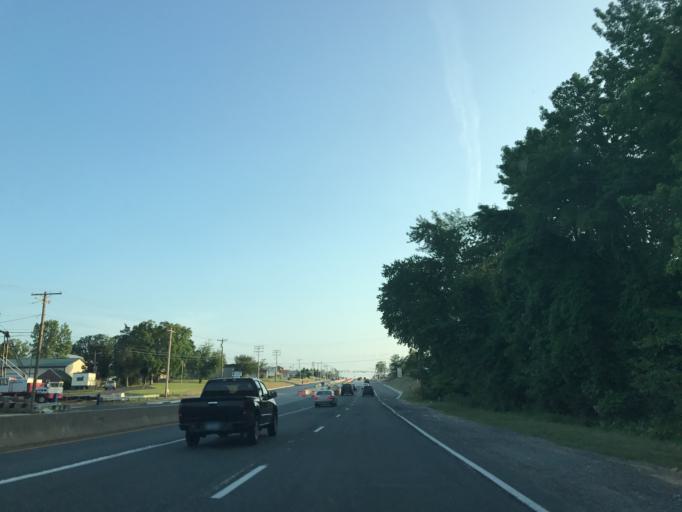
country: US
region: Maryland
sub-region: Baltimore County
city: White Marsh
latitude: 39.3641
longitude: -76.4420
